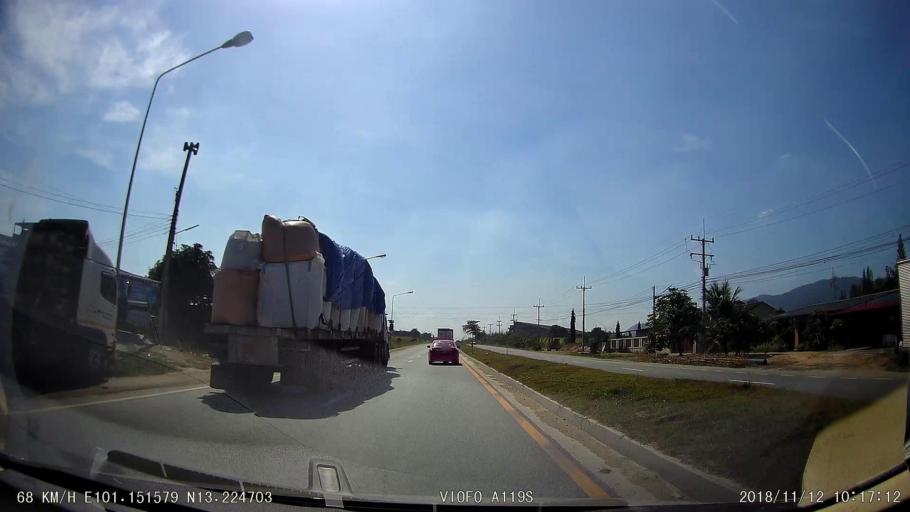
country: TH
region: Chon Buri
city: Ban Bueng
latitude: 13.2242
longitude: 101.1517
